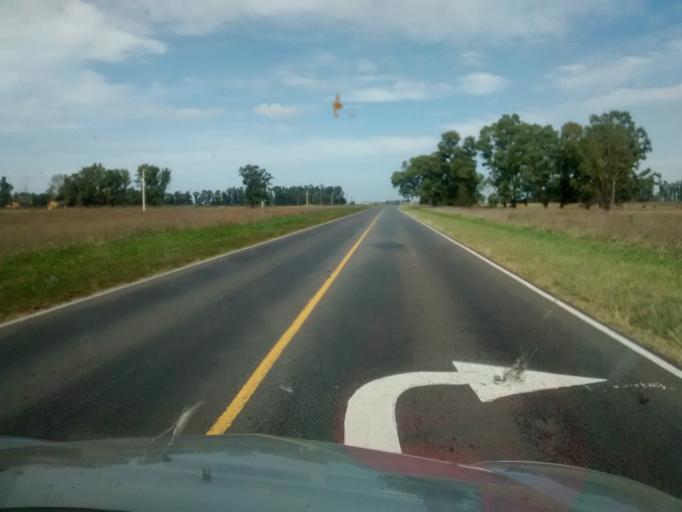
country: AR
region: Buenos Aires
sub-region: Partido de Ayacucho
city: Ayacucho
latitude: -37.1183
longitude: -58.5501
